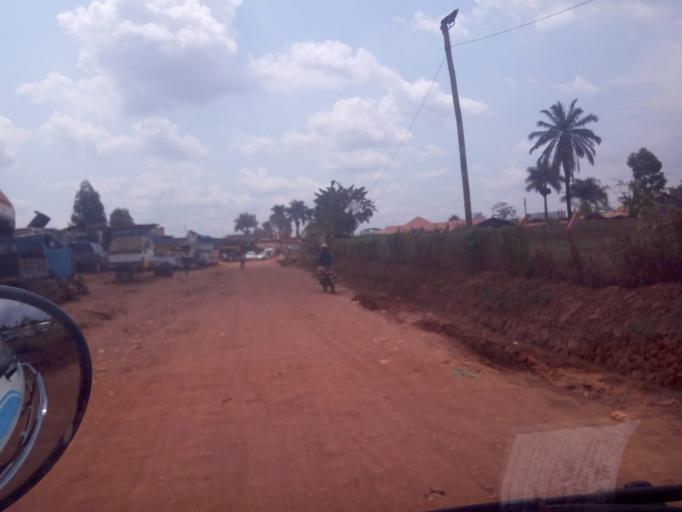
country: UG
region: Central Region
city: Kampala Central Division
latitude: 0.3474
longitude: 32.5591
